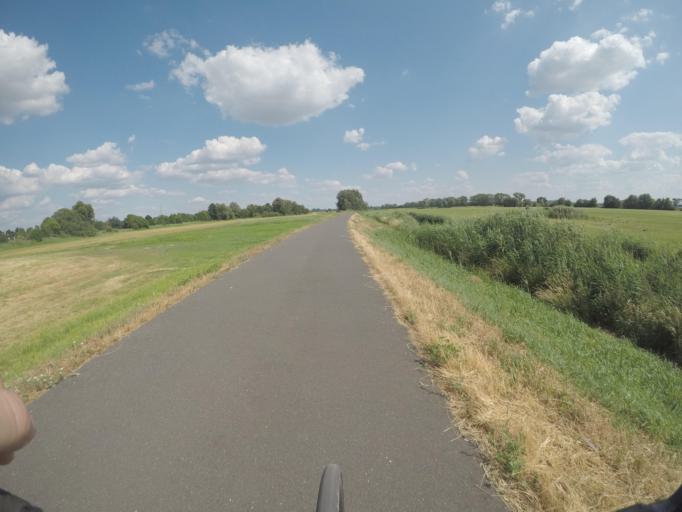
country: DE
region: Brandenburg
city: Ketzin
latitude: 52.4638
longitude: 12.8471
